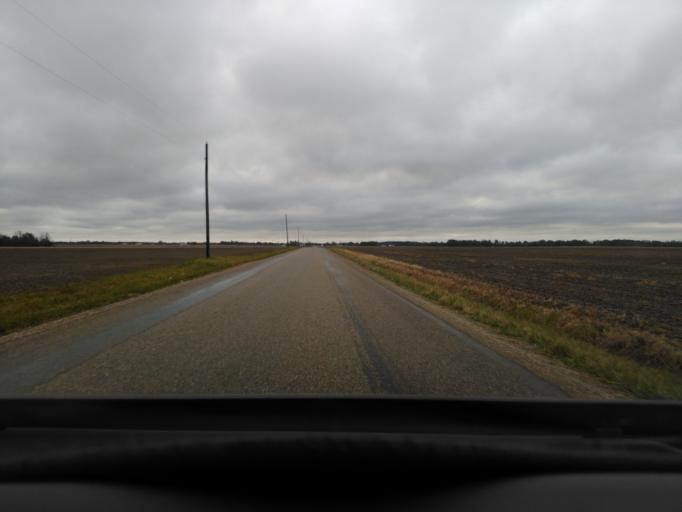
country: US
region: Illinois
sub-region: Effingham County
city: Altamont
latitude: 38.9564
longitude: -88.6634
